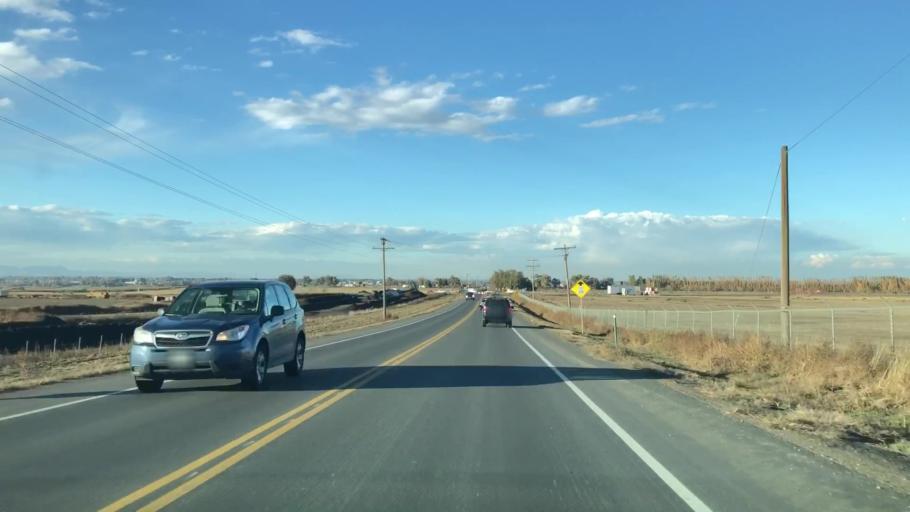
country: US
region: Colorado
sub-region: Larimer County
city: Loveland
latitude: 40.4616
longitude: -105.0204
